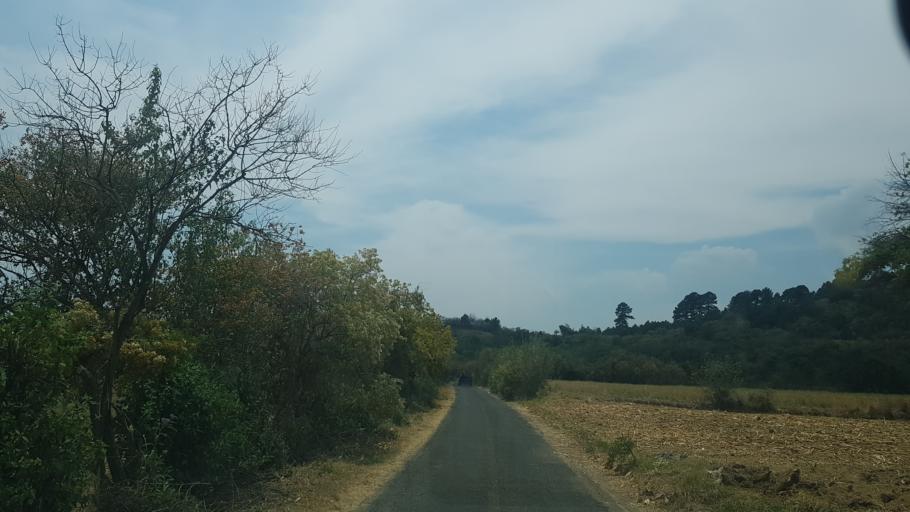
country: MX
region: Puebla
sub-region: Atzitzihuacan
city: Santiago Atzitzihuacan
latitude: 18.8535
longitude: -98.6117
